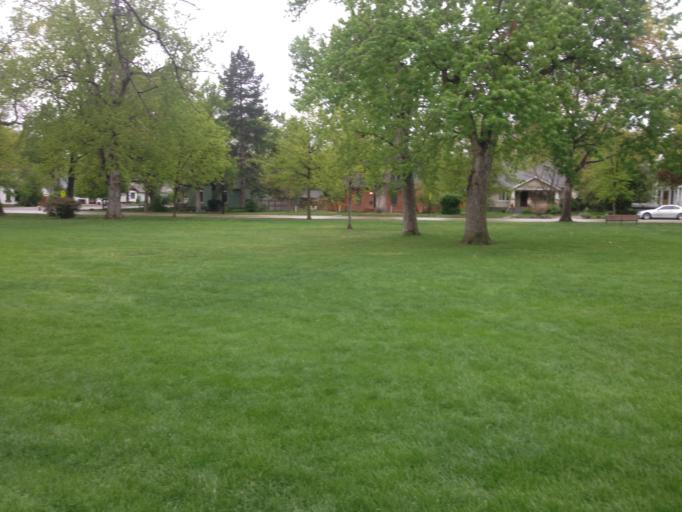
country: US
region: Colorado
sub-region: Boulder County
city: Longmont
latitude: 40.1698
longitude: -105.0975
